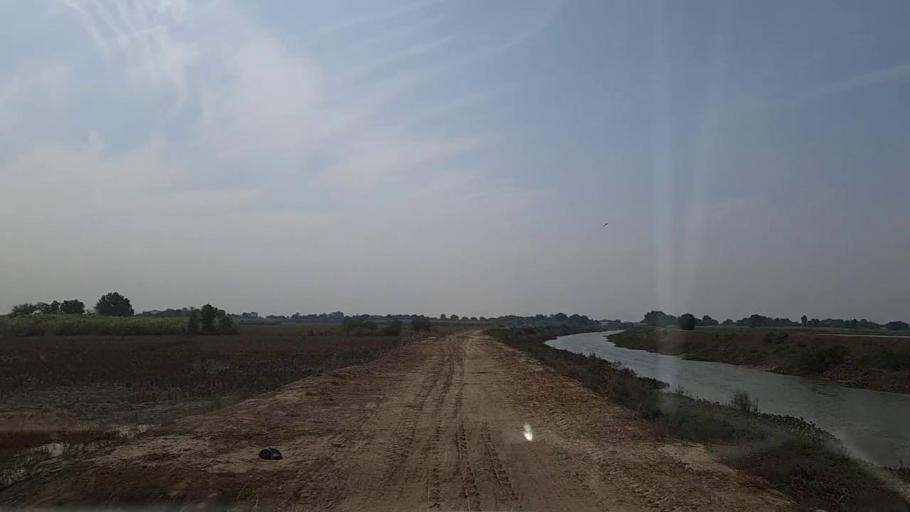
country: PK
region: Sindh
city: Mirpur Batoro
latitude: 24.6445
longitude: 68.2279
